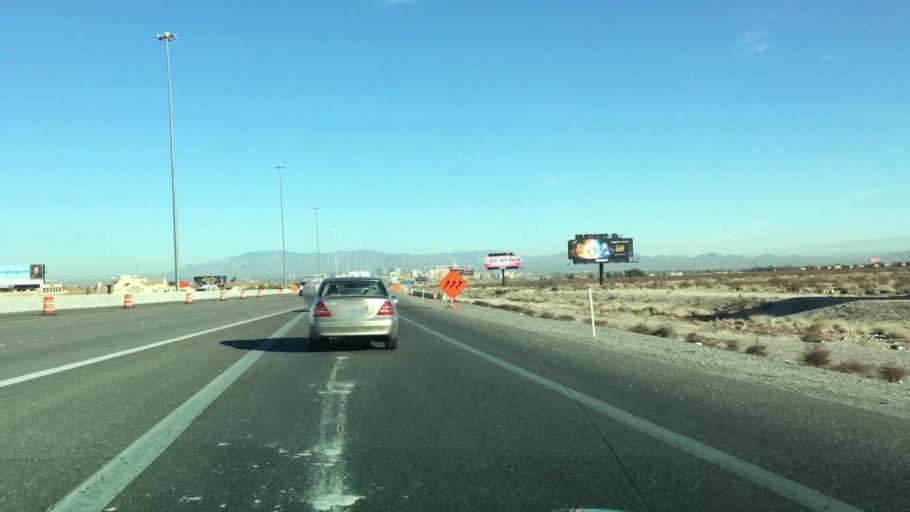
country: US
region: Nevada
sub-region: Clark County
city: Enterprise
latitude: 35.9703
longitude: -115.1810
